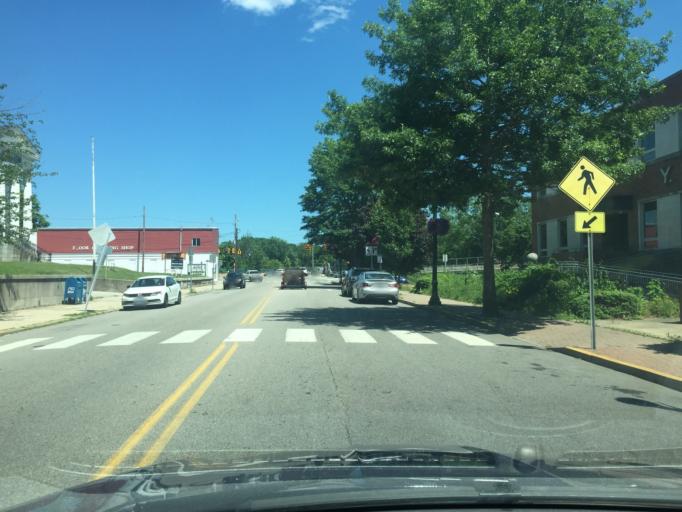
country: US
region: Connecticut
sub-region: New London County
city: Norwich
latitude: 41.5242
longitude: -72.0717
